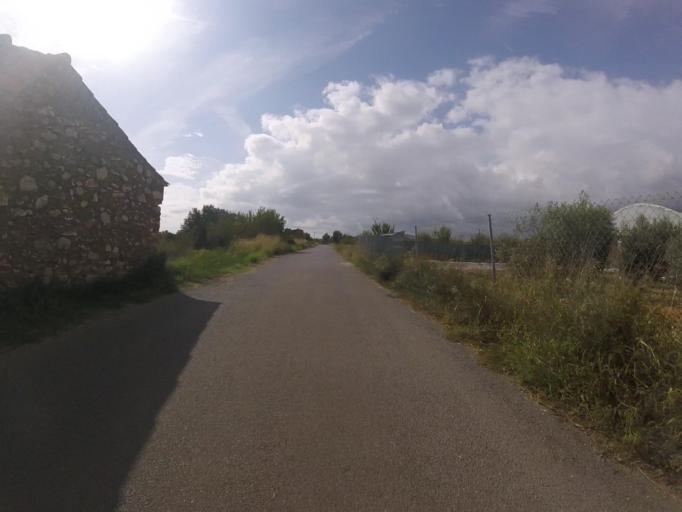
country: ES
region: Valencia
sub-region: Provincia de Castello
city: Orpesa/Oropesa del Mar
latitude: 40.1580
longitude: 0.1680
